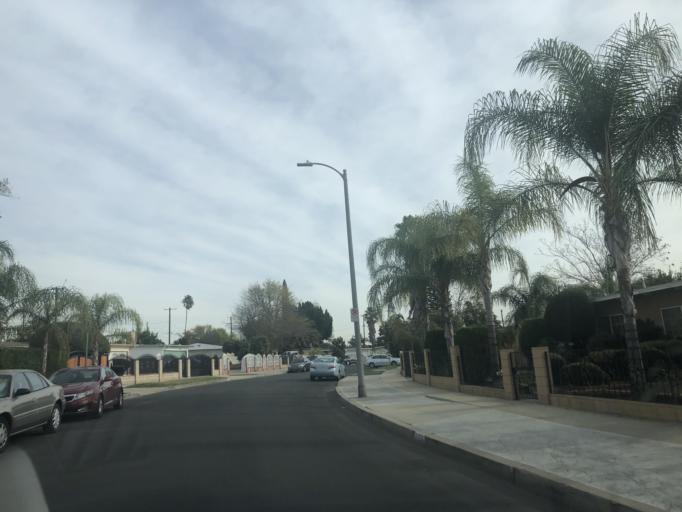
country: US
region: California
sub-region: Los Angeles County
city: San Fernando
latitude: 34.2724
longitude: -118.4362
